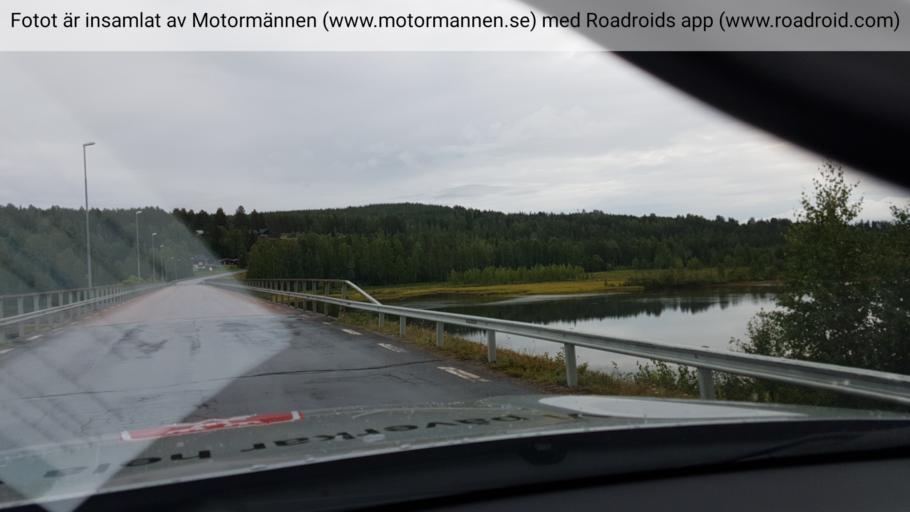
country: SE
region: Norrbotten
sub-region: Alvsbyns Kommun
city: AElvsbyn
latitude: 66.0925
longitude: 20.9316
